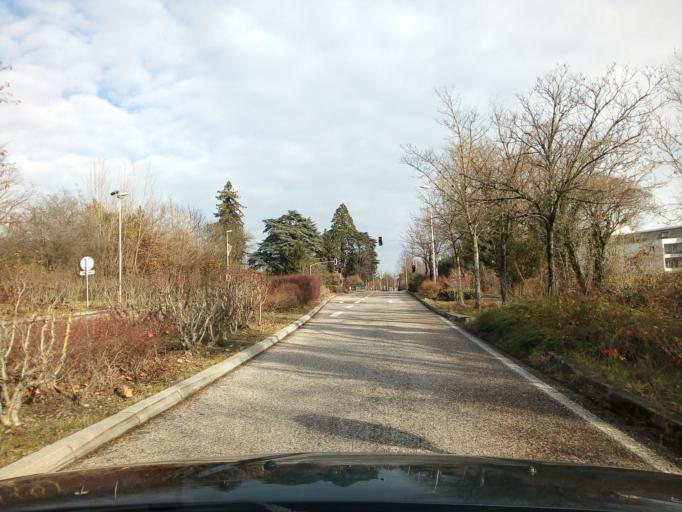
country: FR
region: Rhone-Alpes
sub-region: Departement de l'Isere
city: Corenc
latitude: 45.2130
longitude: 5.7766
